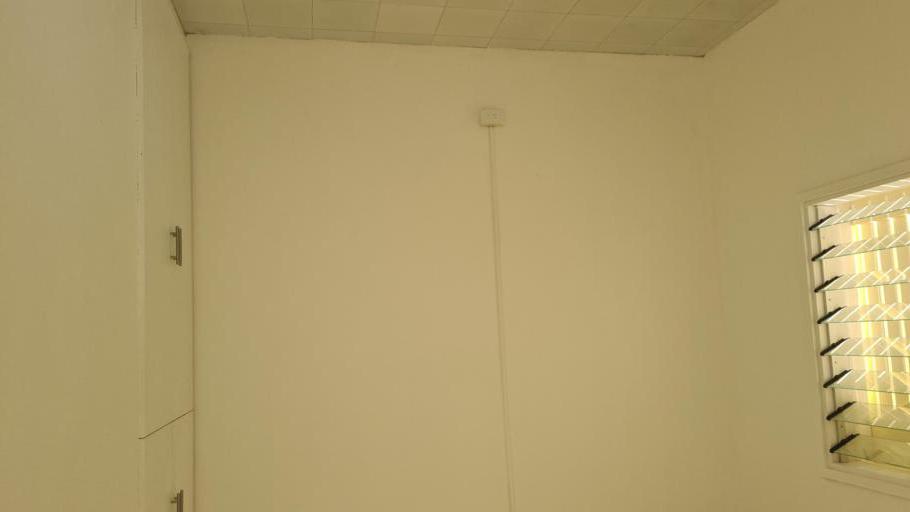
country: VU
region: Malampa
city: Lakatoro
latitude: -16.1167
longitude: 168.1508
